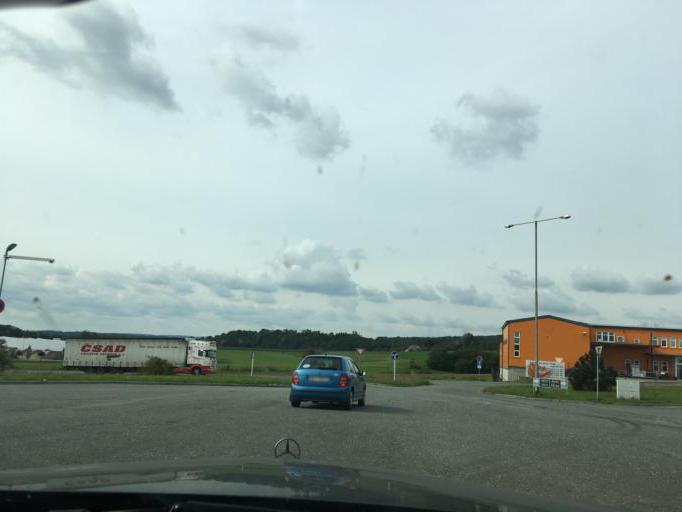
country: CZ
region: Kralovehradecky
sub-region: Okres Nachod
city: Nachod
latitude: 50.3982
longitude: 16.1060
